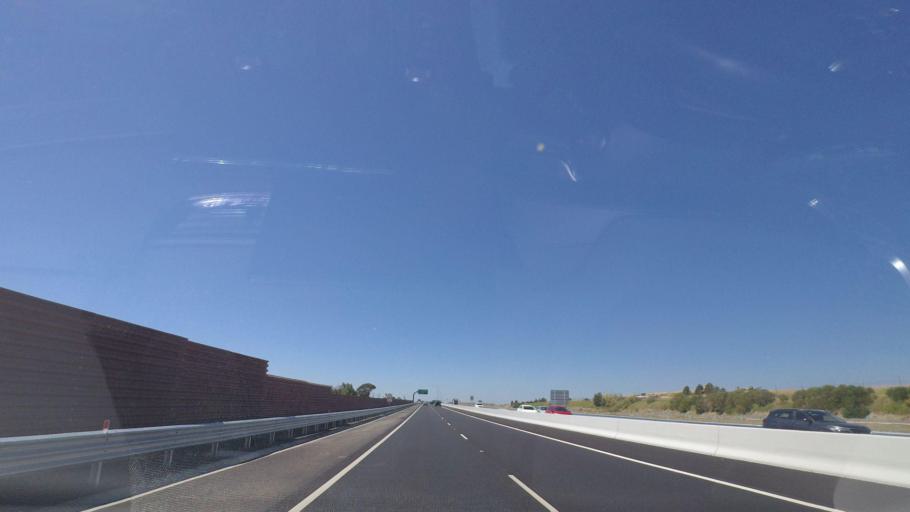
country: AU
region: Victoria
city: Heatherton
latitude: -37.9673
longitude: 145.1166
